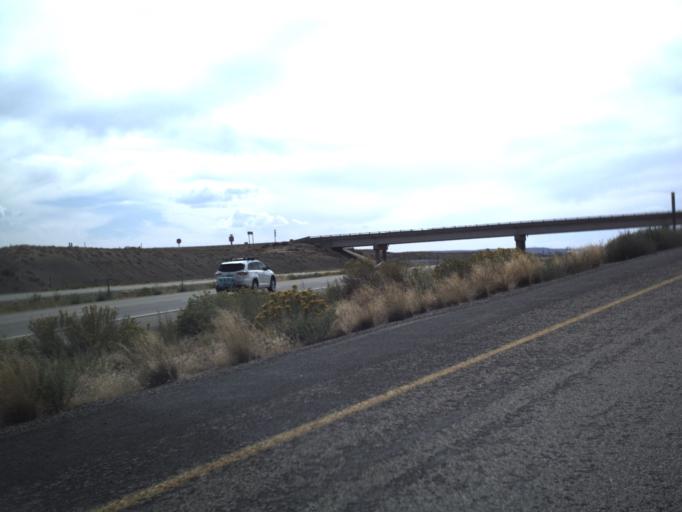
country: US
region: Utah
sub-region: Grand County
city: Moab
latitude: 38.9402
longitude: -109.4052
